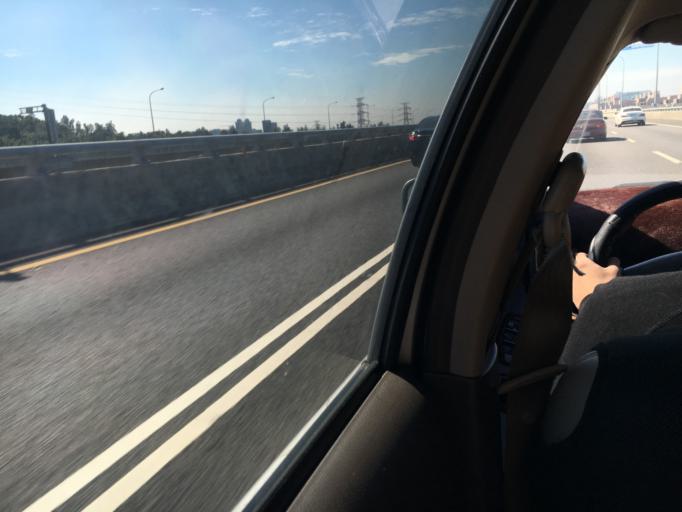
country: TW
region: Taiwan
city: Taoyuan City
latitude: 25.0447
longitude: 121.3106
